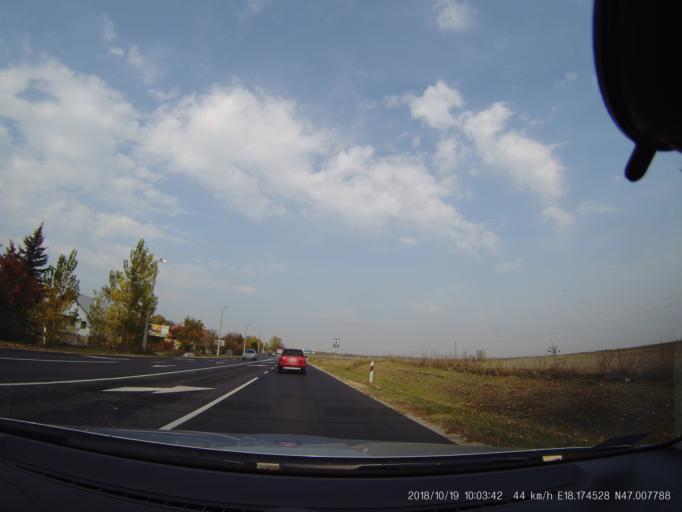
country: HU
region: Fejer
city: Lepseny
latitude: 47.0078
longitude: 18.1745
